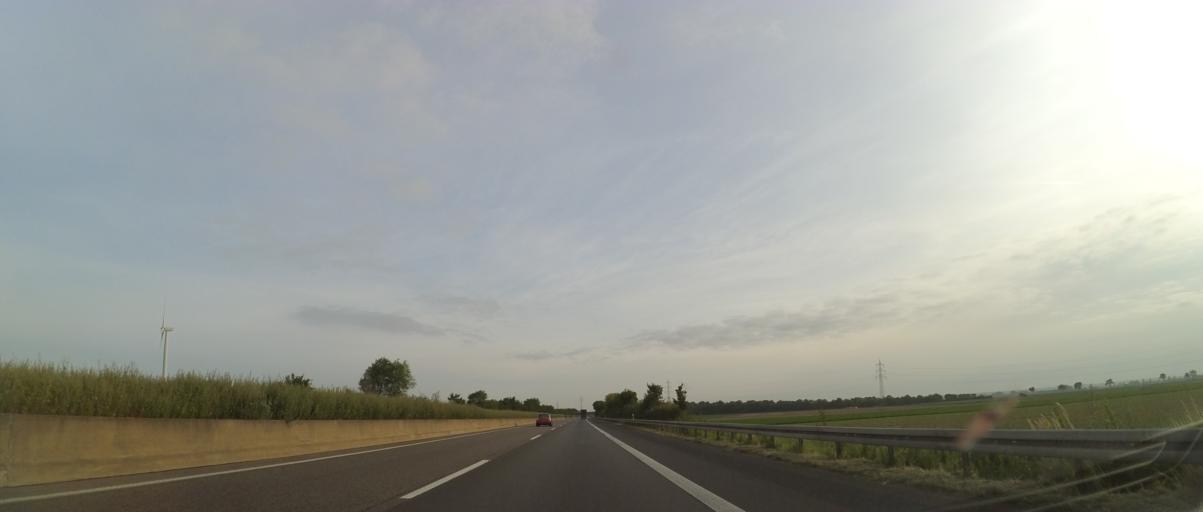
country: DE
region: North Rhine-Westphalia
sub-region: Regierungsbezirk Koln
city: Euskirchen
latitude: 50.7132
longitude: 6.7765
